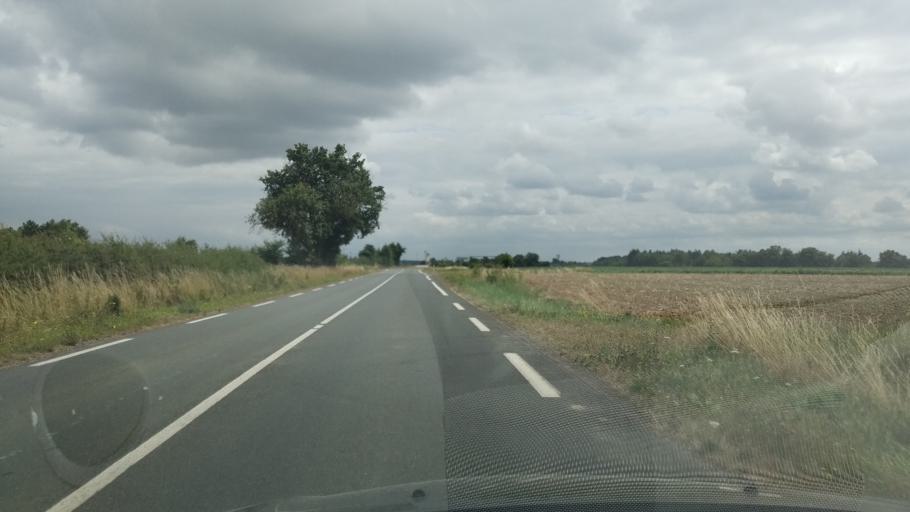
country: FR
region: Poitou-Charentes
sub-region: Departement de la Vienne
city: Saint-Maurice-la-Clouere
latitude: 46.3910
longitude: 0.4004
